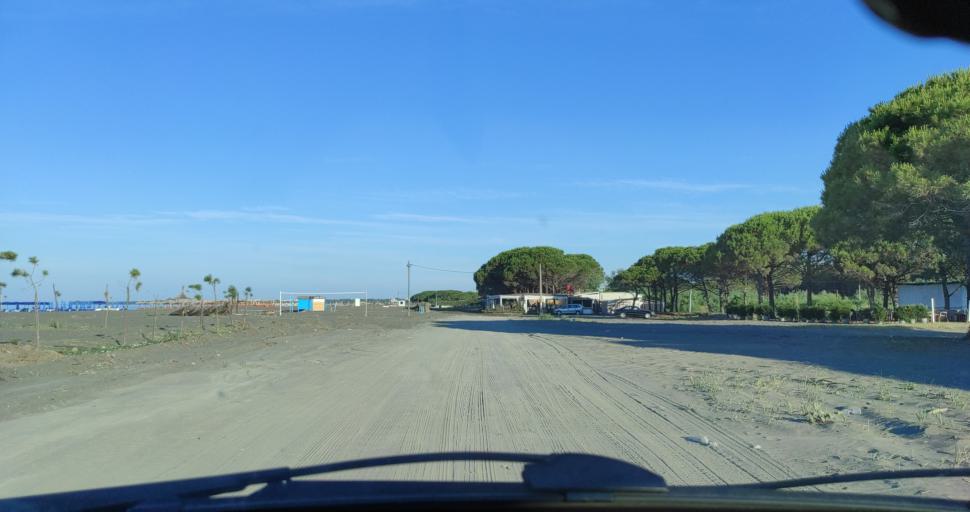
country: AL
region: Shkoder
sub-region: Rrethi i Shkodres
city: Velipoje
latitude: 41.8597
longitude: 19.4408
